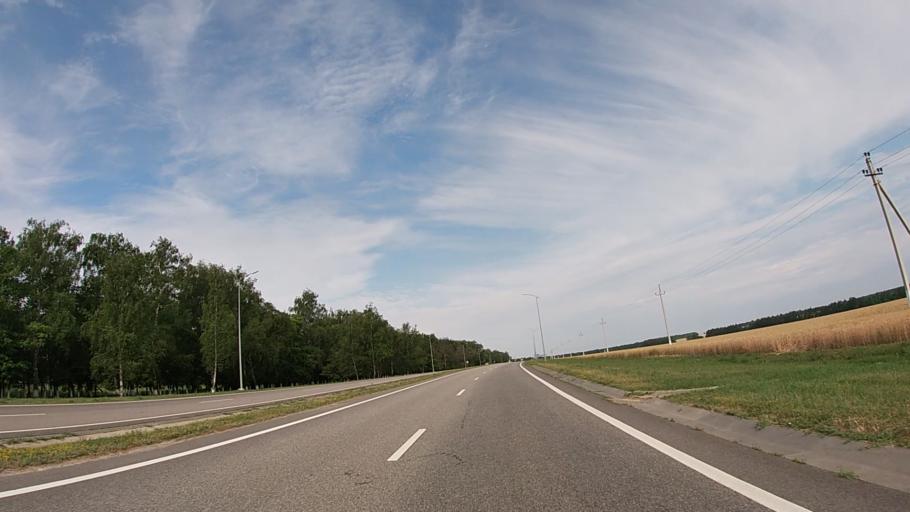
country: RU
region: Belgorod
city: Borisovka
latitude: 50.7495
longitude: 35.9885
